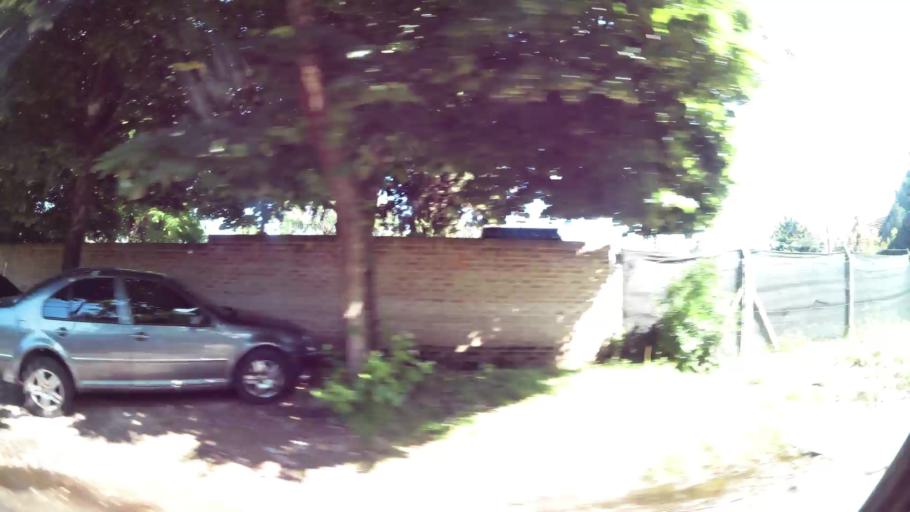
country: AR
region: Buenos Aires
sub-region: Partido de Tigre
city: Tigre
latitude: -34.4852
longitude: -58.5769
